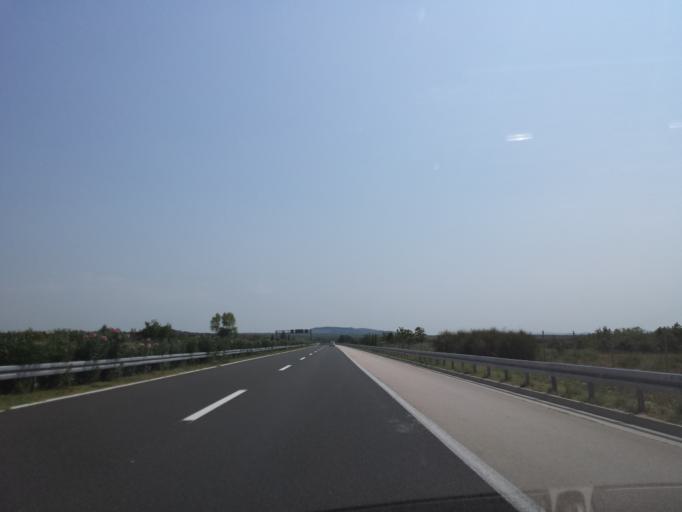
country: HR
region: Zadarska
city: Galovac
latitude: 44.1055
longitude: 15.4594
